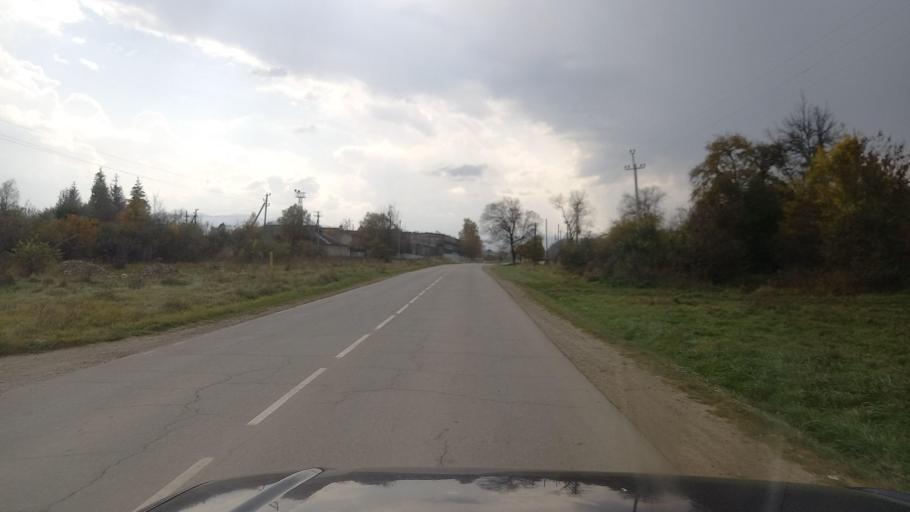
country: RU
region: Krasnodarskiy
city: Psebay
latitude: 44.1416
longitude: 40.8224
